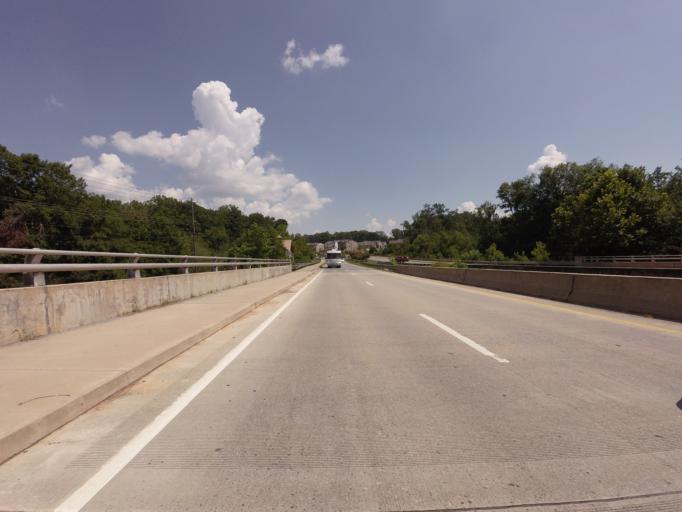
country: US
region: Georgia
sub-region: Fulton County
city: Johns Creek
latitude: 34.0273
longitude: -84.2025
